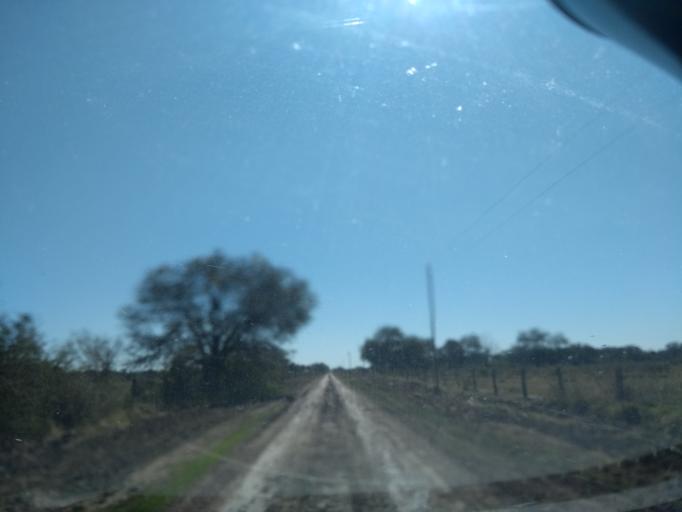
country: AR
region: Chaco
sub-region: Departamento de Quitilipi
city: Quitilipi
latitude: -26.7446
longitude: -60.2378
